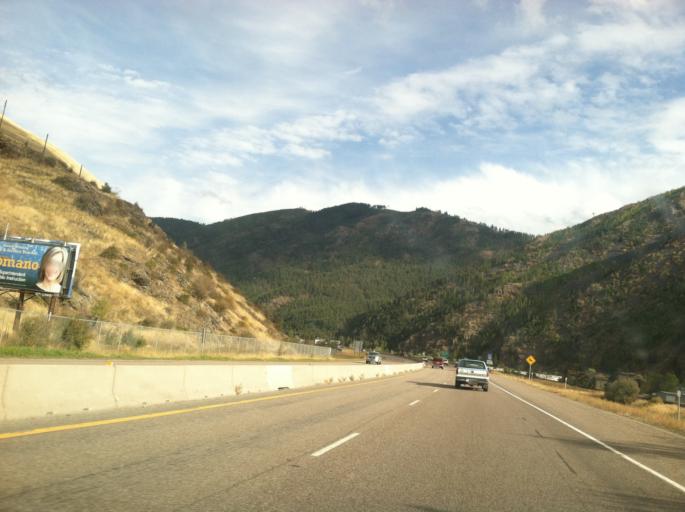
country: US
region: Montana
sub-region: Missoula County
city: Missoula
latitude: 46.8672
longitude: -113.9769
